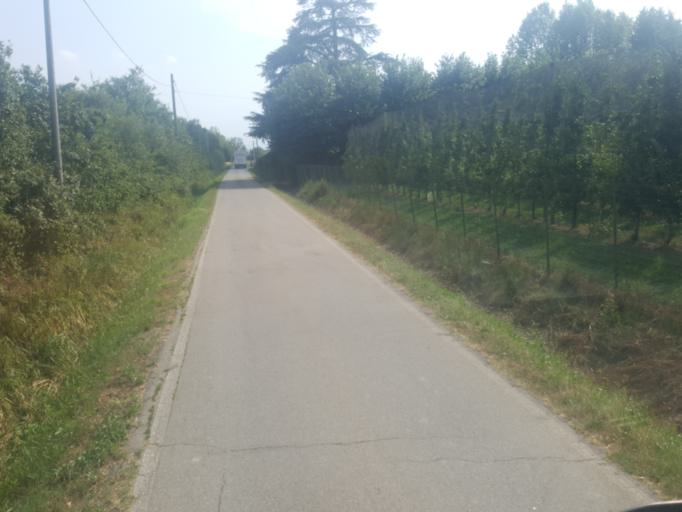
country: IT
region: Emilia-Romagna
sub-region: Provincia di Modena
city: Gaggio
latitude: 44.6400
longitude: 11.0057
